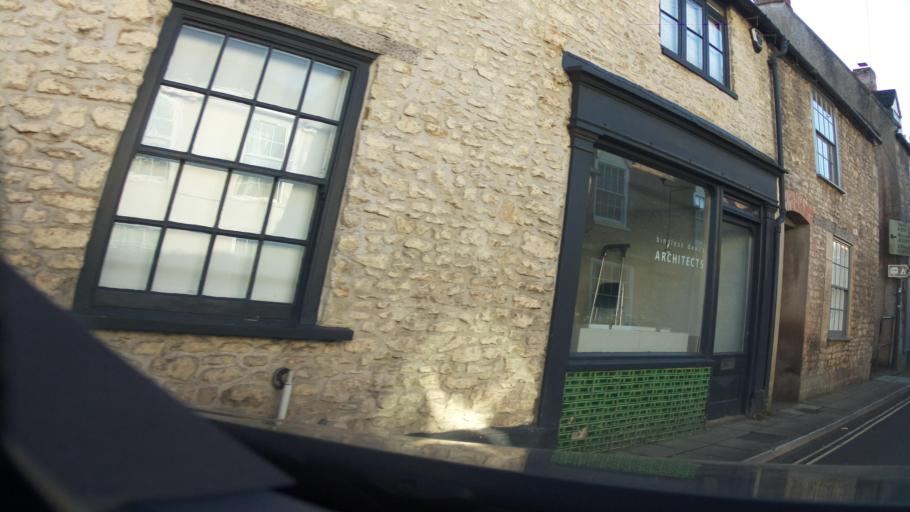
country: GB
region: England
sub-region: Somerset
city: Bruton
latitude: 51.1130
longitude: -2.4516
